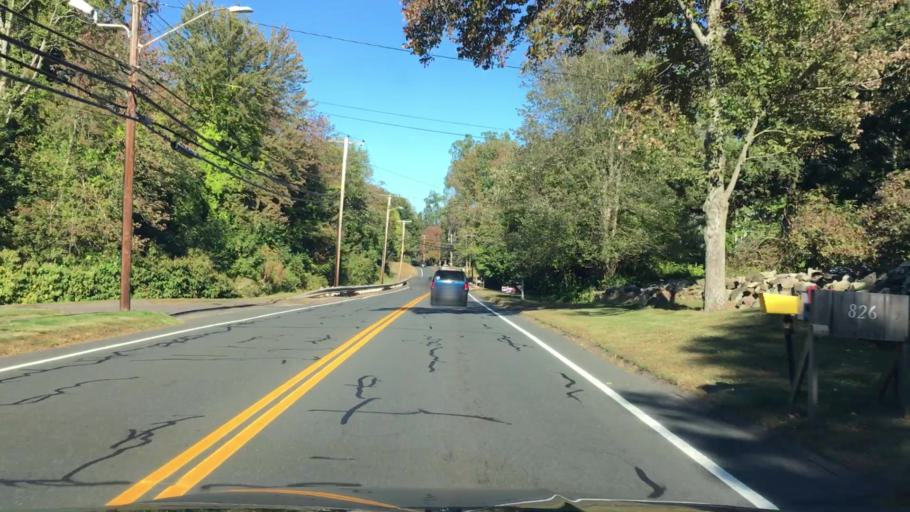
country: US
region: Connecticut
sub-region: Tolland County
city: Rockville
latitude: 41.8427
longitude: -72.4590
